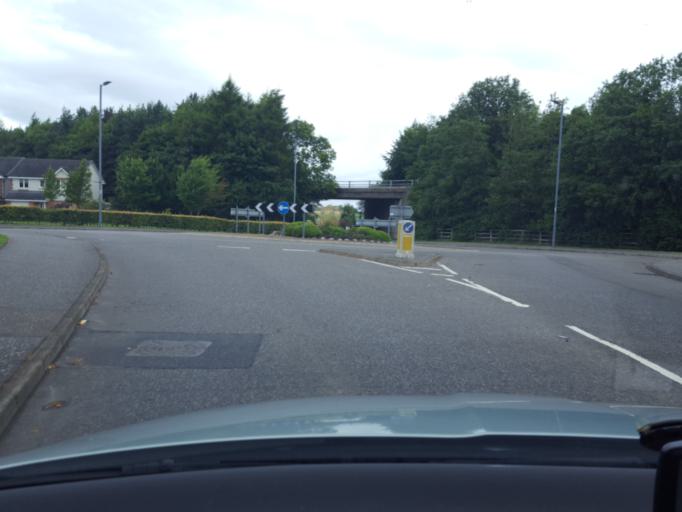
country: GB
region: Scotland
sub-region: Stirling
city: Plean
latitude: 56.0670
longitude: -3.8773
